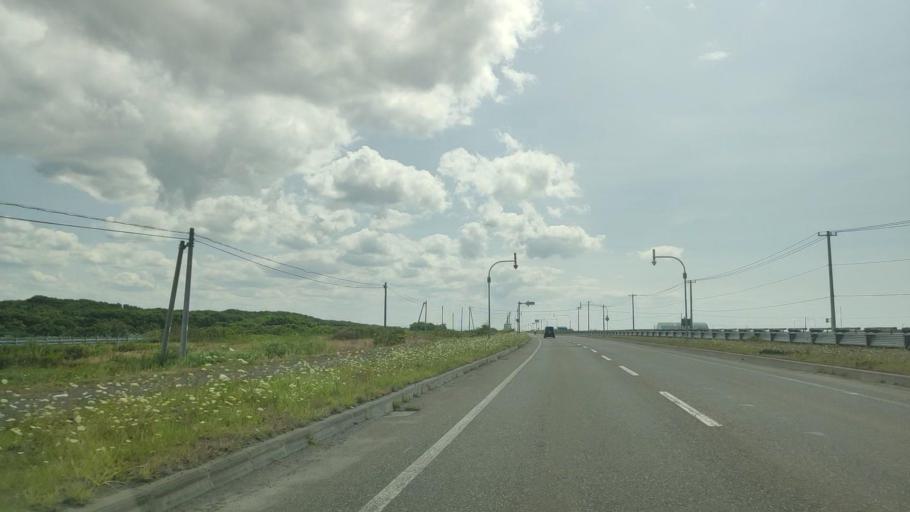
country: JP
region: Hokkaido
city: Makubetsu
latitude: 44.8700
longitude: 141.7524
